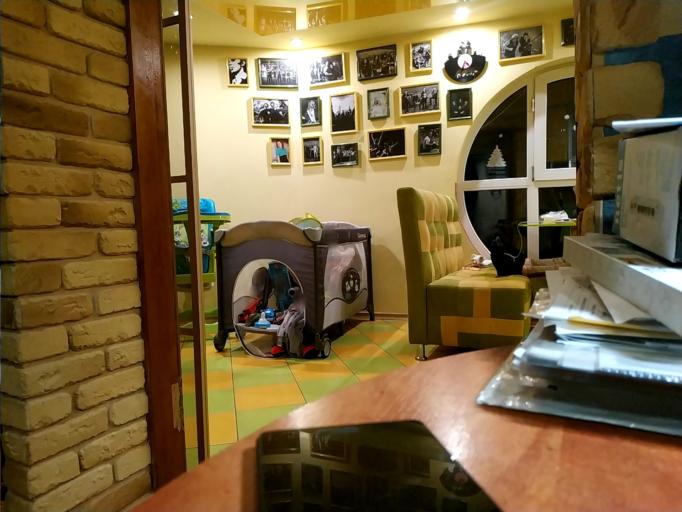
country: RU
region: Orjol
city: Naryshkino
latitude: 53.0439
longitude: 35.6806
